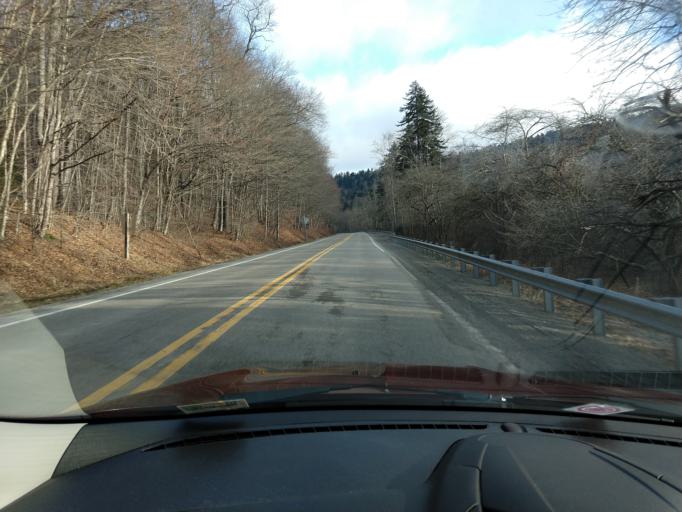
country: US
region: West Virginia
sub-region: Randolph County
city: Elkins
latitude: 38.6224
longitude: -79.8674
